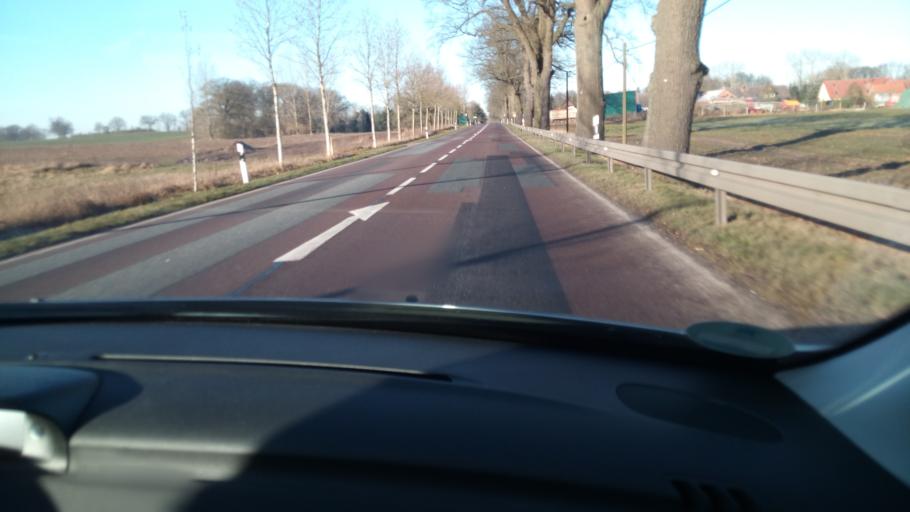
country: DE
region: Mecklenburg-Vorpommern
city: Robel
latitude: 53.3470
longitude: 12.5234
